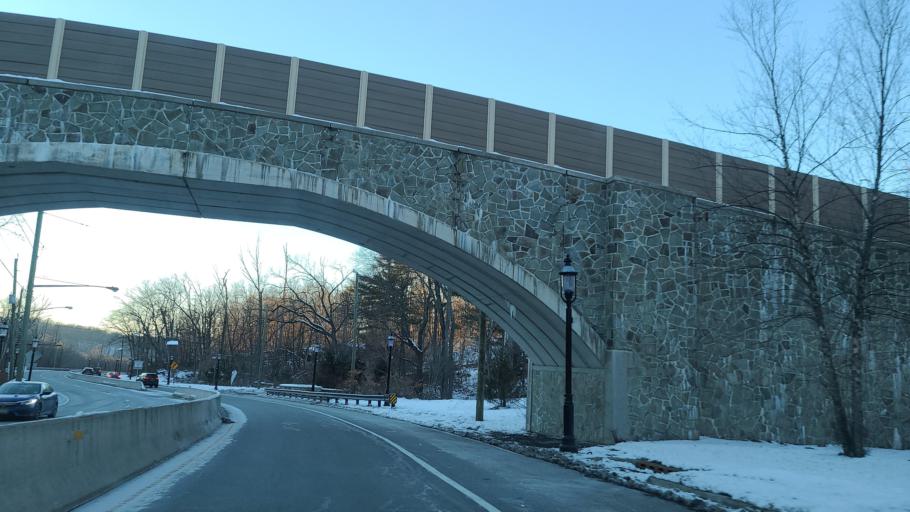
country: US
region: New Jersey
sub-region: Essex County
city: Maplewood
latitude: 40.7485
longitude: -74.2837
